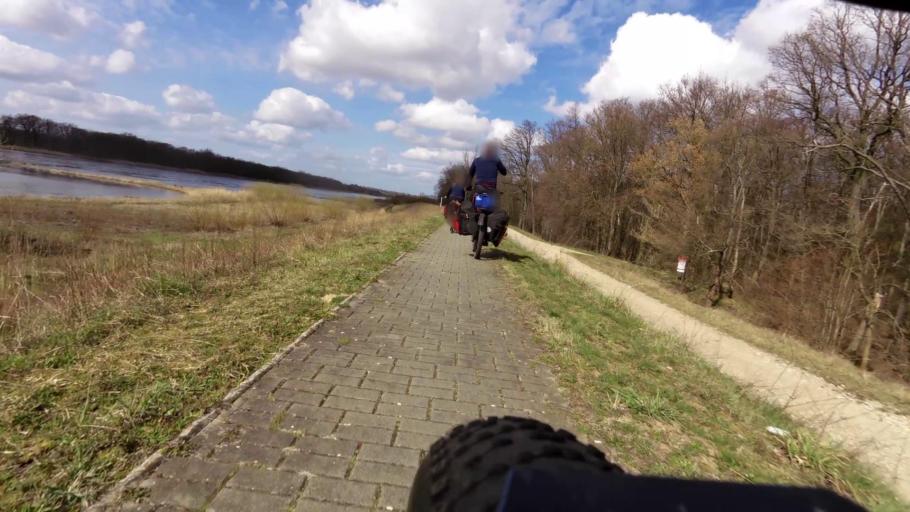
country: PL
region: Lubusz
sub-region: Powiat slubicki
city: Slubice
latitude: 52.3822
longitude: 14.5493
